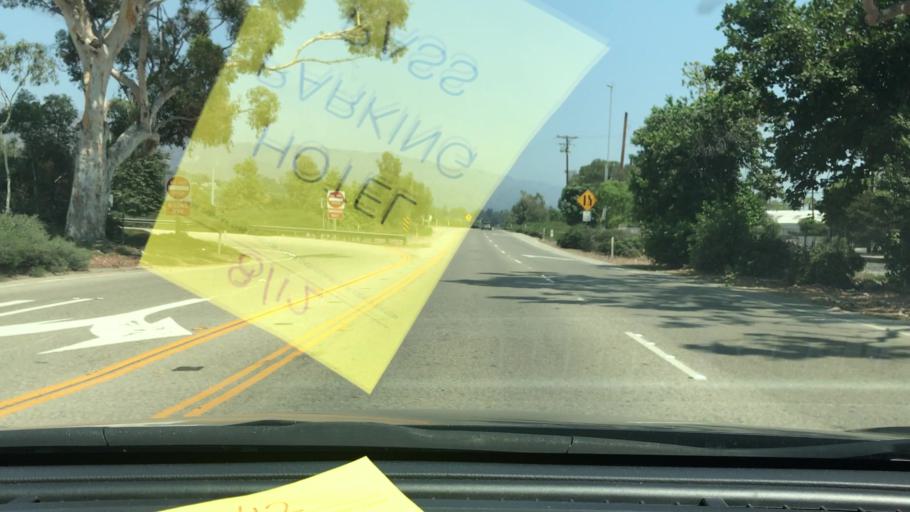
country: US
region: California
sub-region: Santa Barbara County
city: Santa Barbara
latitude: 34.4190
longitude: -119.6739
